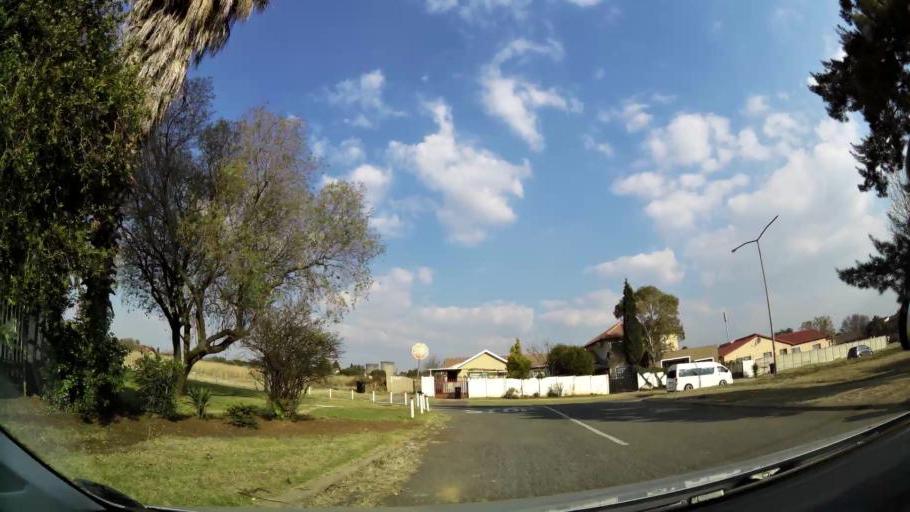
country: ZA
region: Gauteng
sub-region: City of Johannesburg Metropolitan Municipality
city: Modderfontein
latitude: -26.1029
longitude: 28.1876
